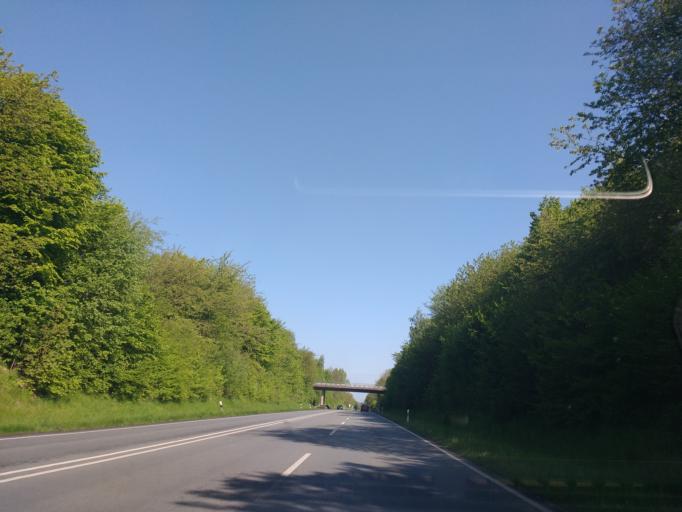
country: DE
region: North Rhine-Westphalia
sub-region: Regierungsbezirk Detmold
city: Detmold
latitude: 51.9346
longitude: 8.9214
